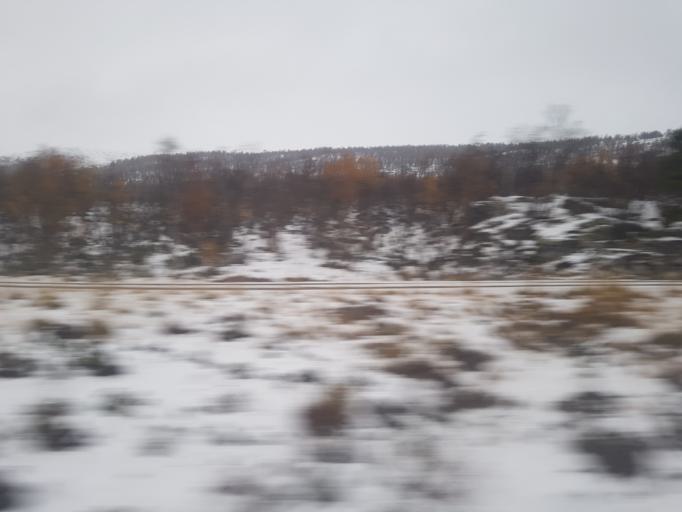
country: NO
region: Oppland
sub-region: Dovre
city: Dovre
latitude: 62.1781
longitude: 9.4557
